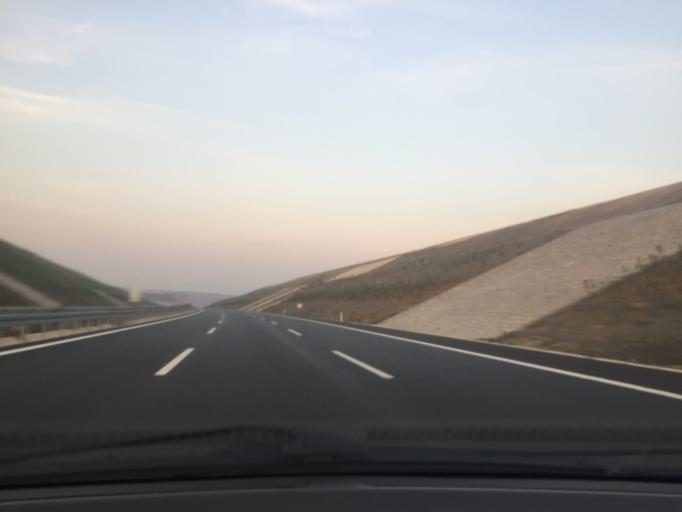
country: TR
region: Bursa
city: Mahmudiye
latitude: 40.2775
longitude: 28.5374
